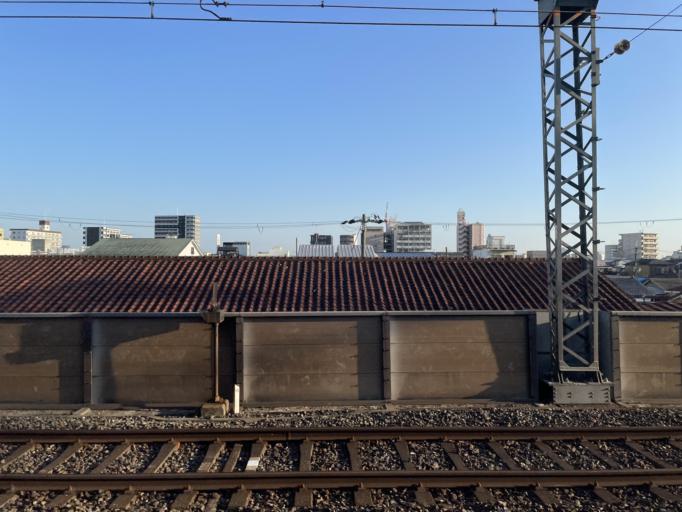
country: JP
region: Osaka
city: Osaka-shi
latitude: 34.6650
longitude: 135.5478
